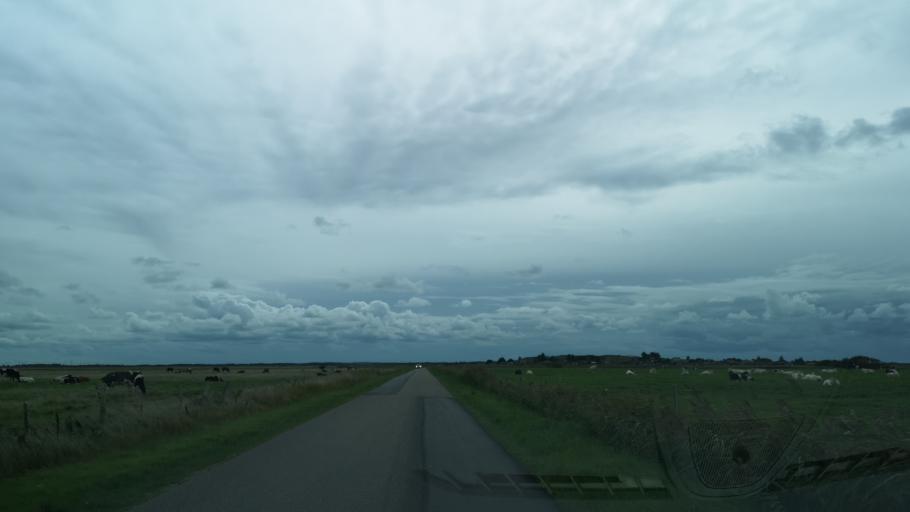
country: DK
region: Central Jutland
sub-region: Ringkobing-Skjern Kommune
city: Hvide Sande
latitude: 55.8595
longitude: 8.2201
